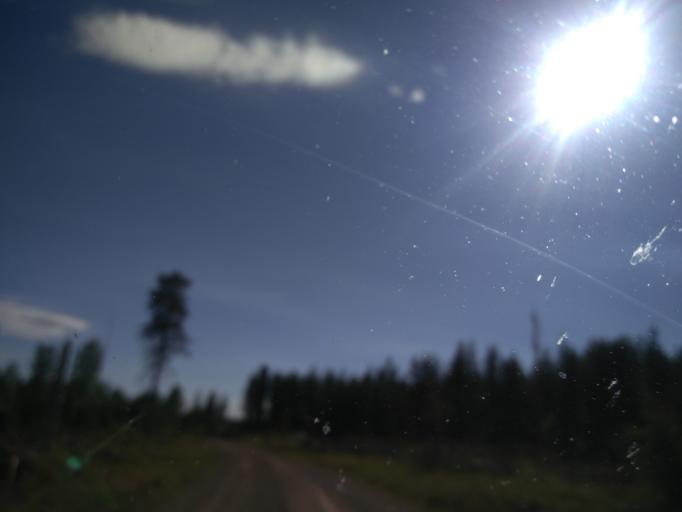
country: SE
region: Vaesternorrland
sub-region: Ange Kommun
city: Fransta
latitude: 62.2278
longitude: 16.2895
